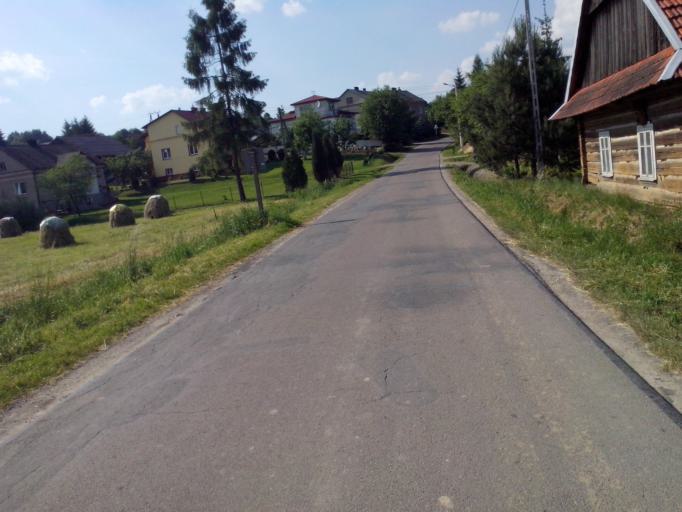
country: PL
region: Subcarpathian Voivodeship
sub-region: Powiat brzozowski
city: Blizne
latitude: 49.7410
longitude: 21.9752
